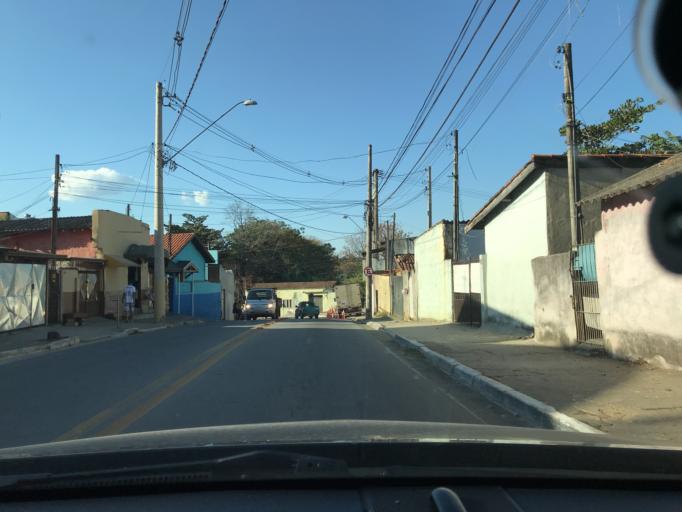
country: BR
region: Sao Paulo
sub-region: Sao Jose Dos Campos
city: Sao Jose dos Campos
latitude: -23.1569
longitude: -45.9026
